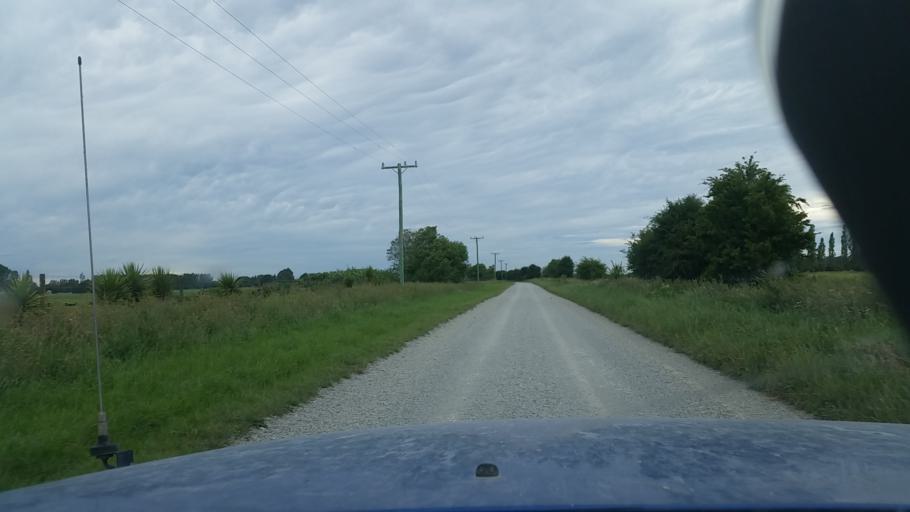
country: NZ
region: Canterbury
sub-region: Ashburton District
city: Ashburton
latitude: -43.8274
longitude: 171.6433
